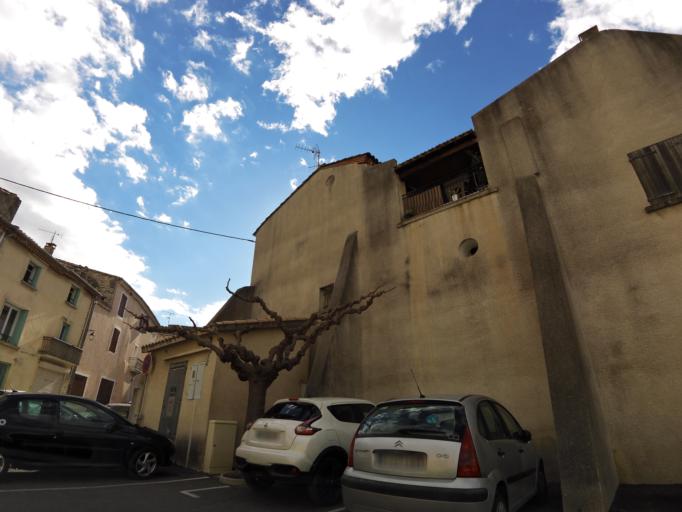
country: FR
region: Languedoc-Roussillon
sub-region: Departement du Gard
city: Calvisson
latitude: 43.7853
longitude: 4.1900
